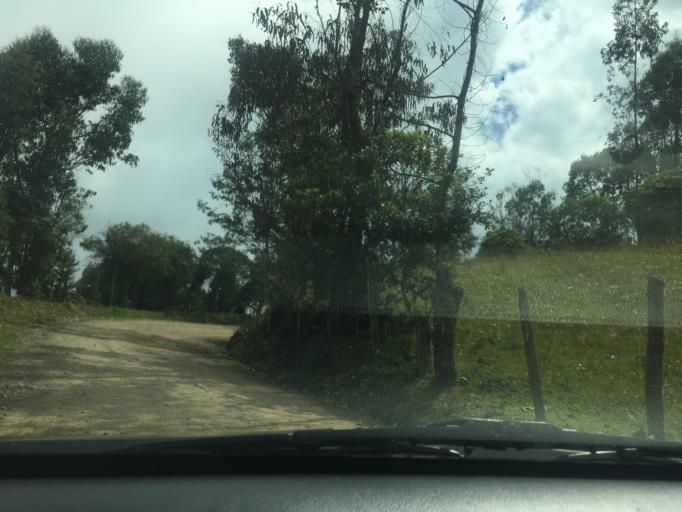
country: CO
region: Cundinamarca
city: Zipacon
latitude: 4.7854
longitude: -74.3785
